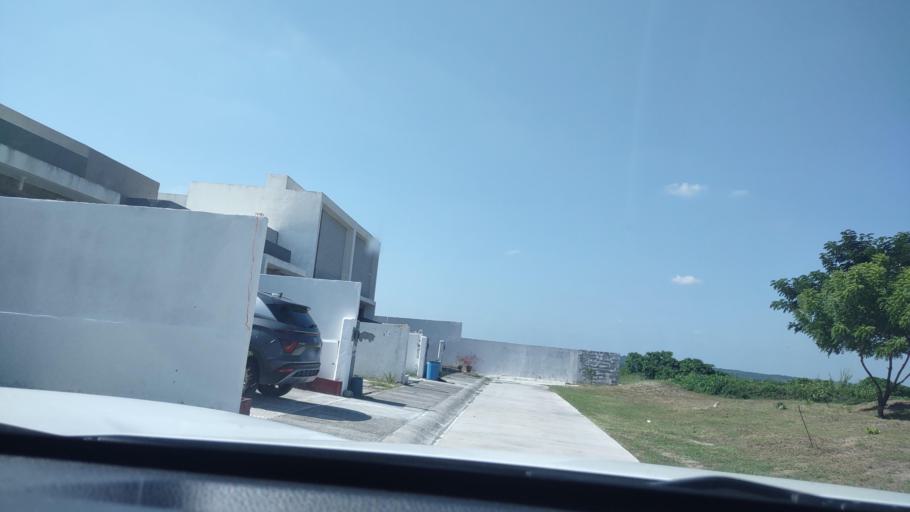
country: MX
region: Veracruz
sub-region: Veracruz
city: Fraccionamiento Geovillas los Pinos
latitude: 19.2192
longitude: -96.2341
